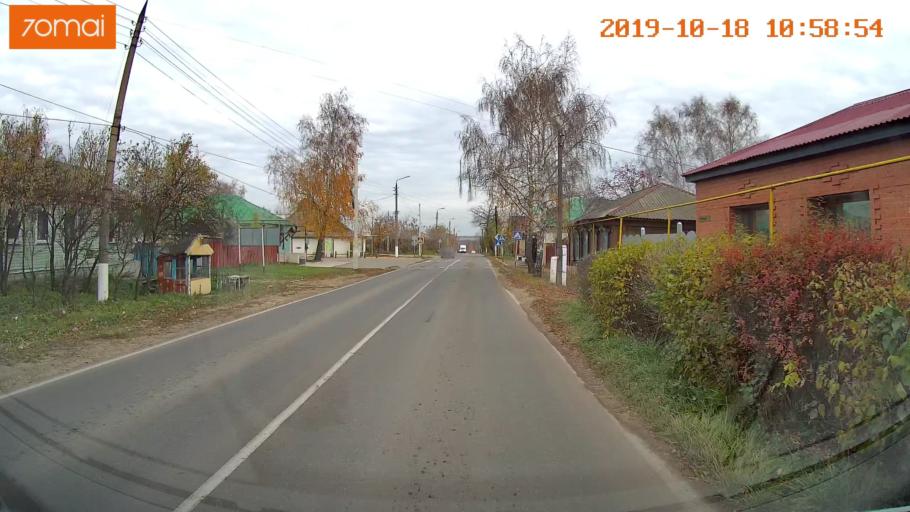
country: RU
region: Tula
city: Yepifan'
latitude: 53.8265
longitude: 38.5539
